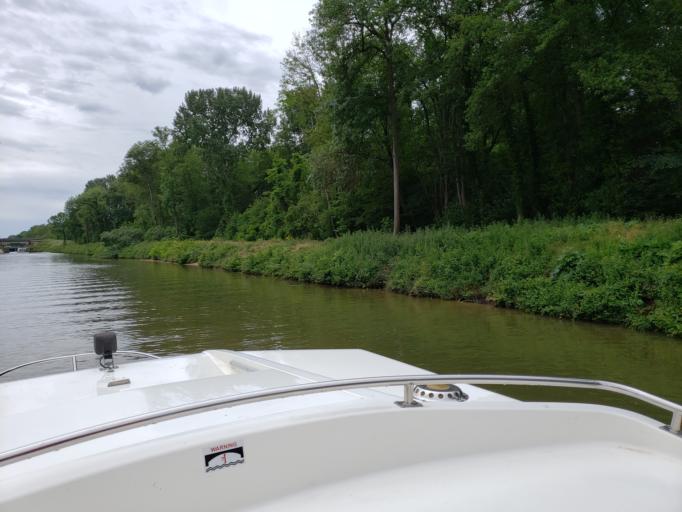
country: FR
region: Bourgogne
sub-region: Departement de l'Yonne
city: Appoigny
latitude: 47.8998
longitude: 3.5355
